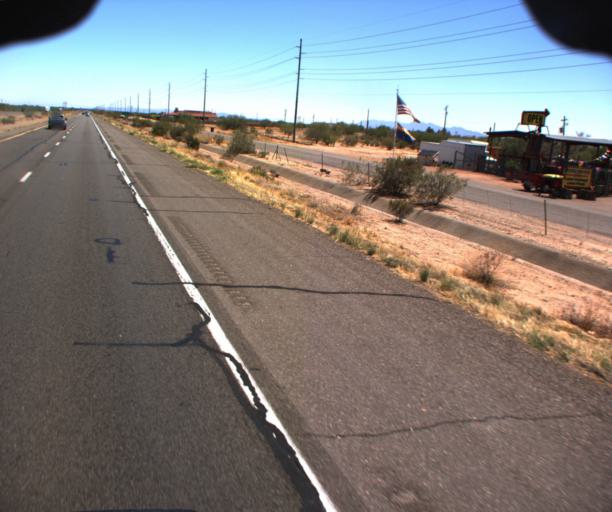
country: US
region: Arizona
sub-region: Maricopa County
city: Sun City West
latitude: 33.7085
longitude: -112.4399
